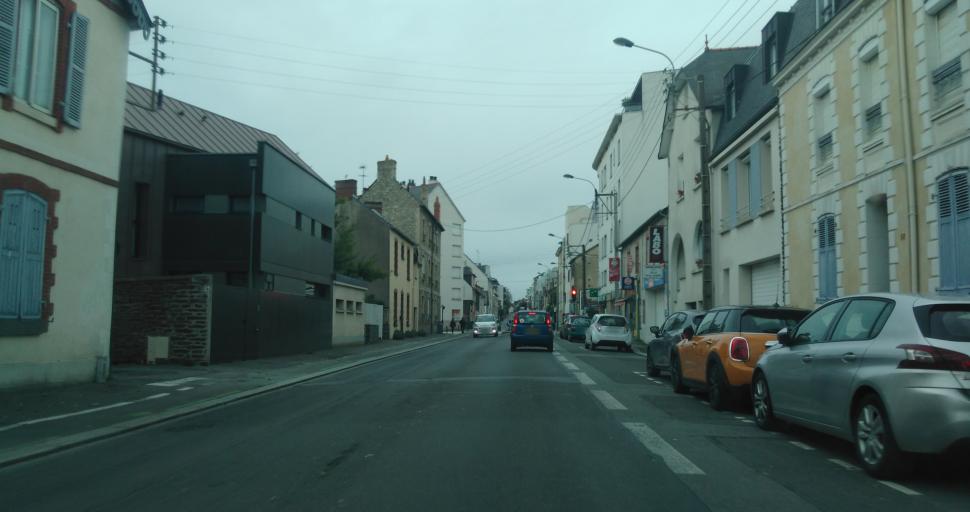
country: FR
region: Brittany
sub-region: Departement d'Ille-et-Vilaine
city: Rennes
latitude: 48.1175
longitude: -1.6593
